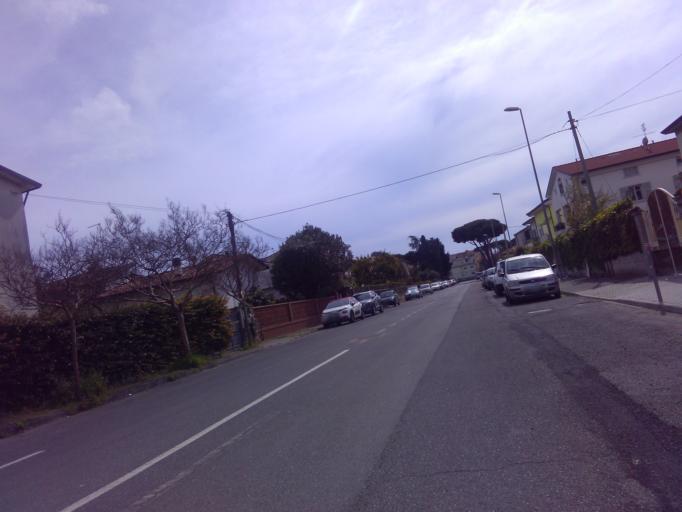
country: IT
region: Tuscany
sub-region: Provincia di Massa-Carrara
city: Marina di Carrara
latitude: 44.0463
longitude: 10.0400
